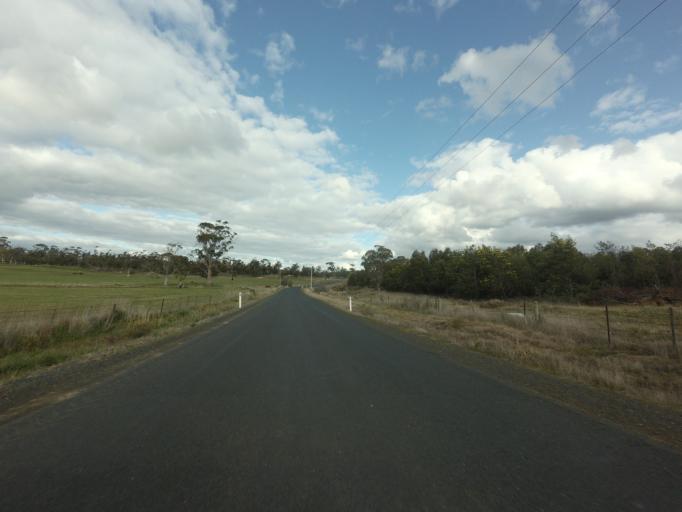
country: AU
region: Tasmania
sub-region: Northern Midlands
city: Longford
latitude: -41.8356
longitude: 147.2097
